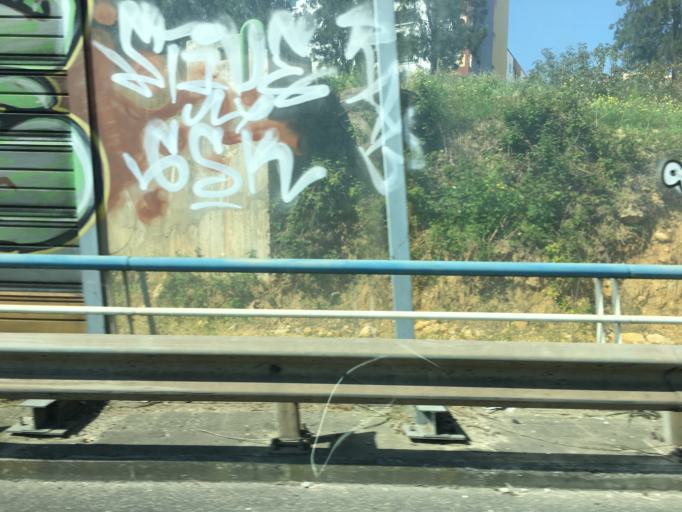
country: PT
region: Lisbon
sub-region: Loures
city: Sacavem
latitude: 38.7945
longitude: -9.1174
